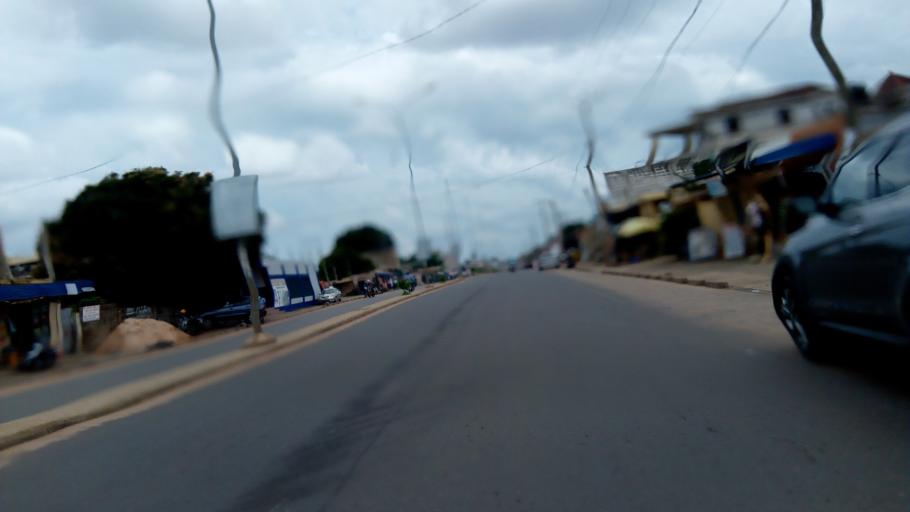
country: TG
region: Maritime
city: Lome
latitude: 6.2081
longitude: 1.1813
